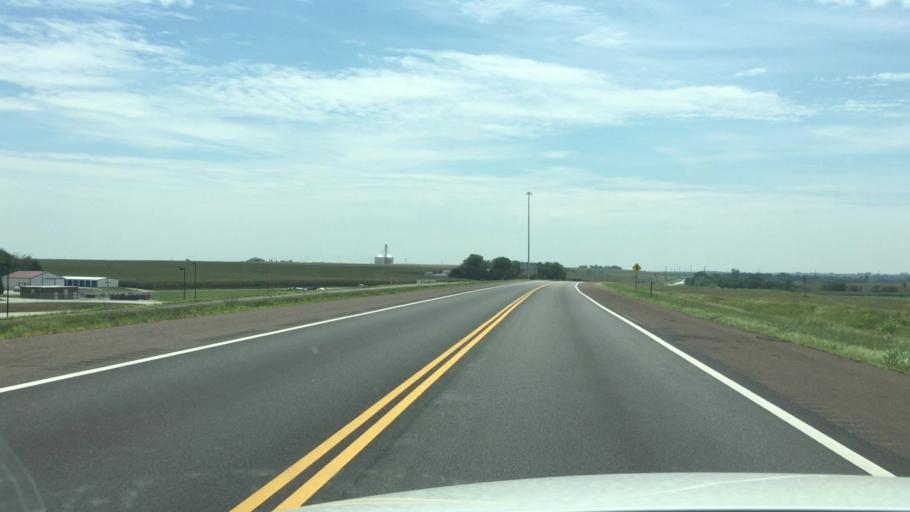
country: US
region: Kansas
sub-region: Nemaha County
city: Sabetha
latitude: 39.8394
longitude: -95.7360
